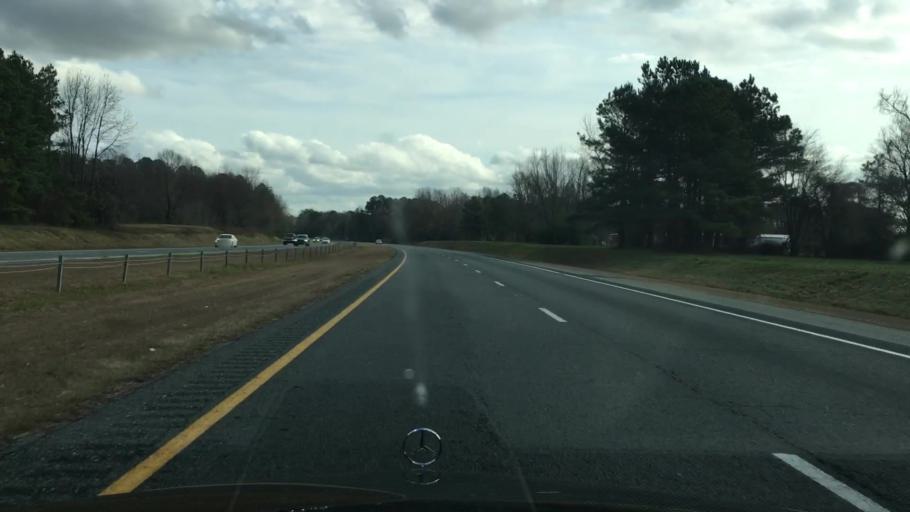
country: US
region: North Carolina
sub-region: Sampson County
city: Clinton
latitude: 35.2138
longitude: -78.3282
